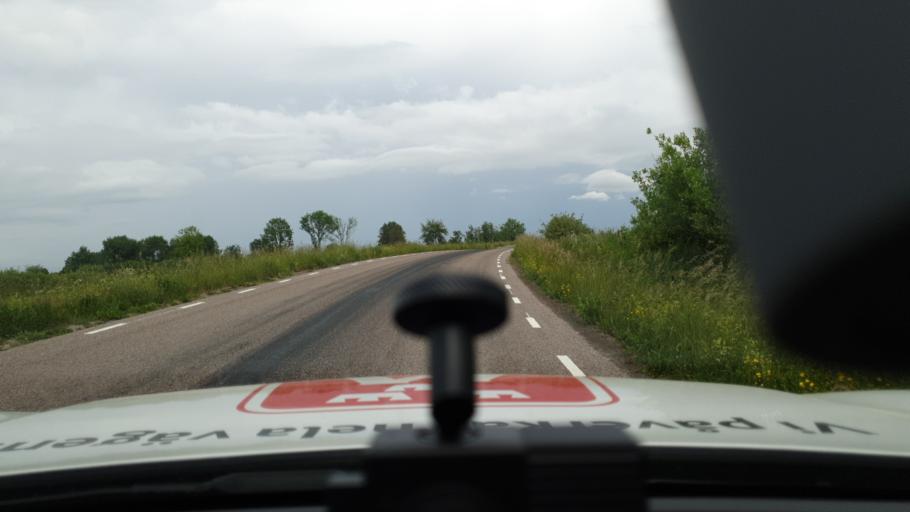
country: SE
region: Vaestra Goetaland
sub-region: Falkopings Kommun
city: Akarp
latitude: 58.1864
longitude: 13.7027
